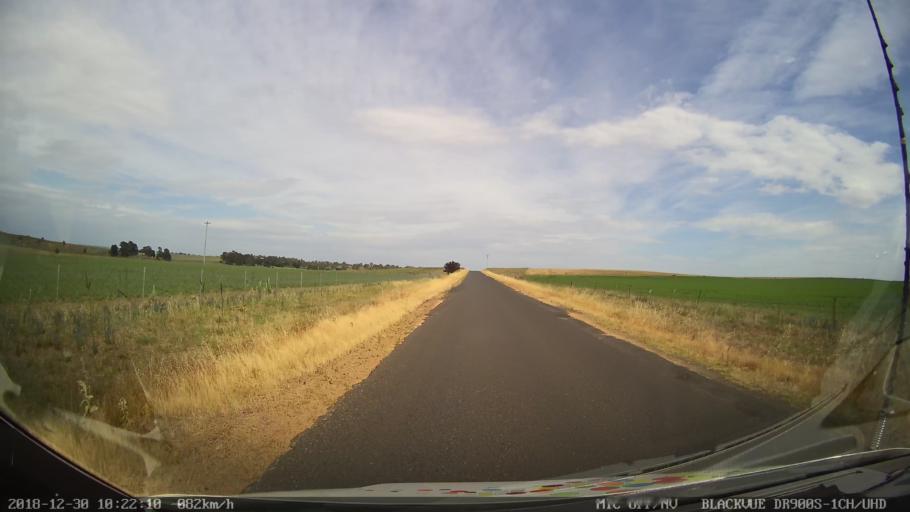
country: AU
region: New South Wales
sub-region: Snowy River
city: Berridale
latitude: -36.5458
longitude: 148.9986
